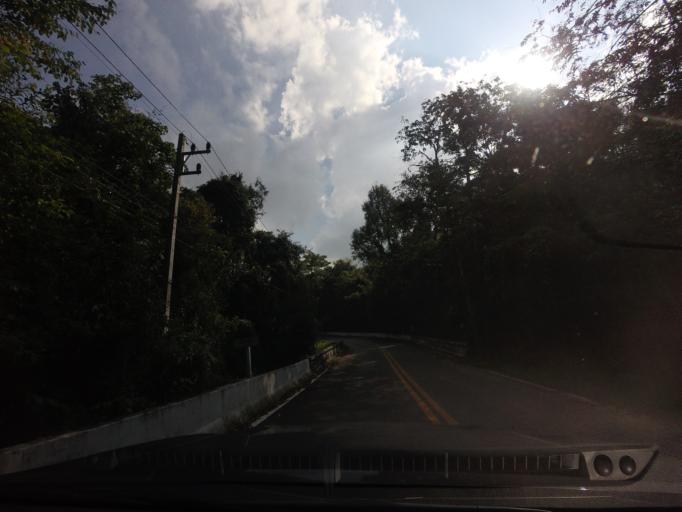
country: TH
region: Phitsanulok
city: Nakhon Thai
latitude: 16.9921
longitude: 101.0126
